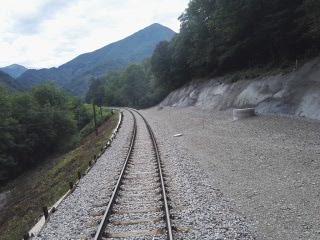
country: SI
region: Cerkno
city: Cerkno
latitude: 46.1613
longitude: 13.8765
